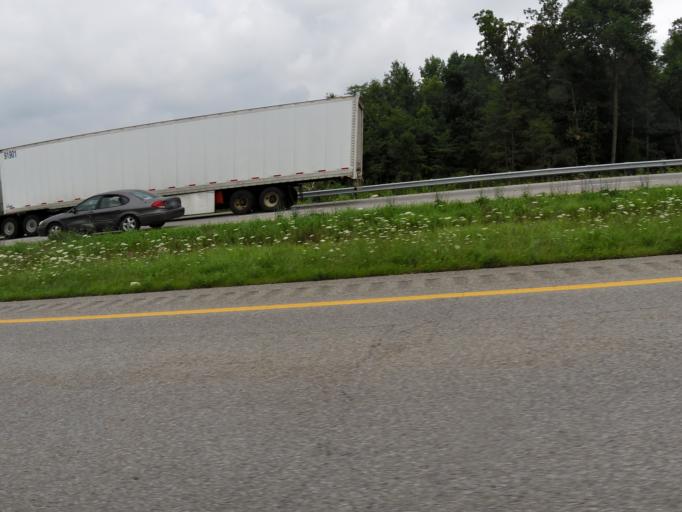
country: US
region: Kentucky
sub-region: Ohio County
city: Beaver Dam
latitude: 37.3306
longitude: -86.9674
